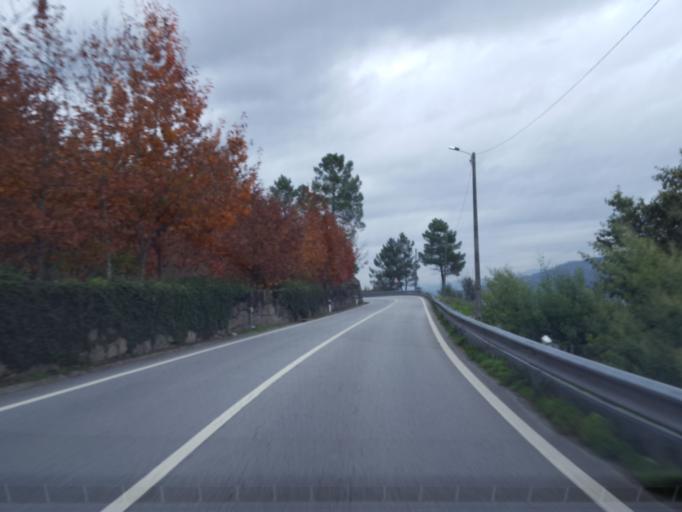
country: PT
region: Porto
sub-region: Marco de Canaveses
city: Marco de Canavezes
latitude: 41.1647
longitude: -8.1453
